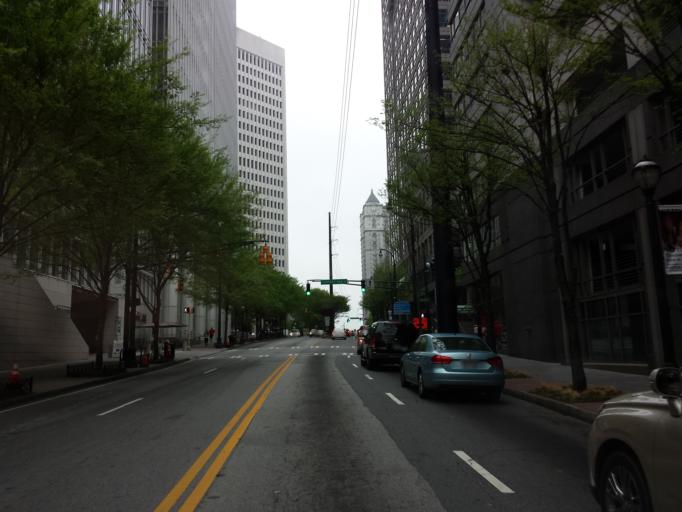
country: US
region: Georgia
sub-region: Fulton County
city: Atlanta
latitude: 33.7866
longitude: -84.3848
